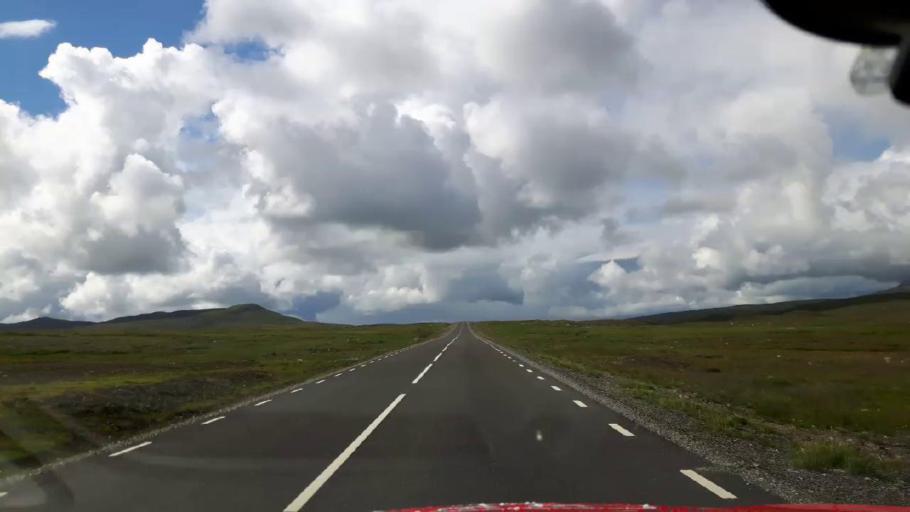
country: NO
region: Nordland
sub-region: Hattfjelldal
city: Hattfjelldal
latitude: 65.0688
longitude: 14.3913
